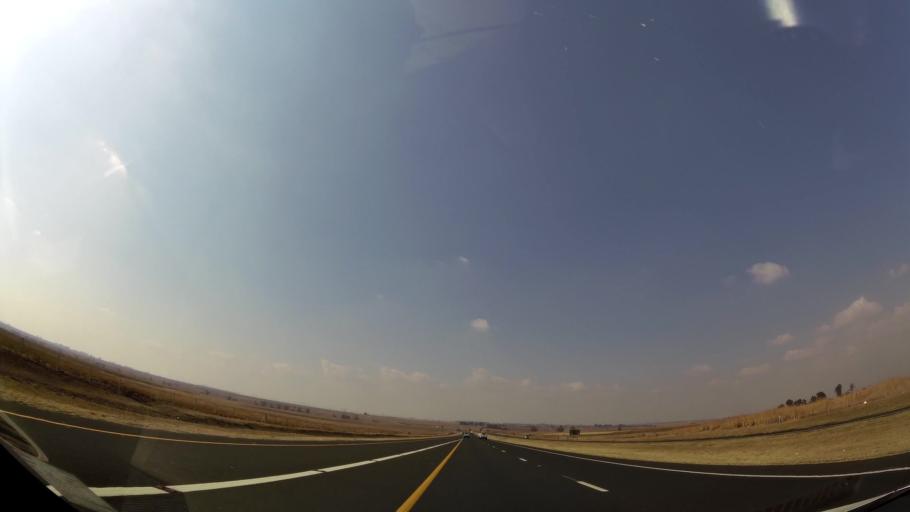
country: ZA
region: Gauteng
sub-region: Ekurhuleni Metropolitan Municipality
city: Springs
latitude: -26.1627
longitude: 28.4481
